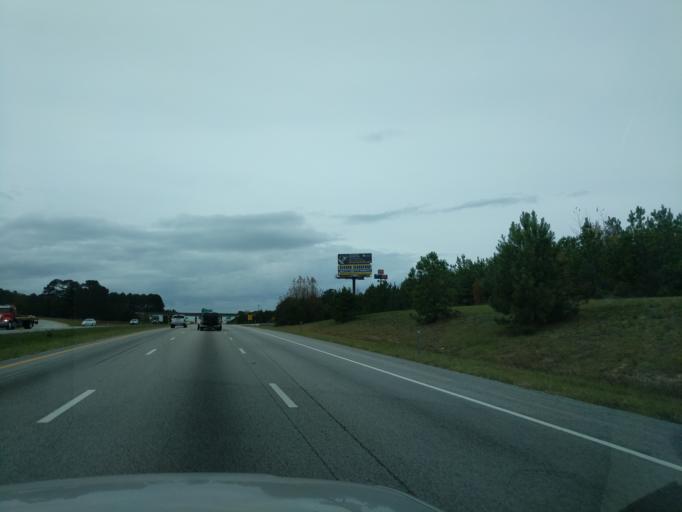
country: US
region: South Carolina
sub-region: Laurens County
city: Clinton
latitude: 34.5047
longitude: -81.8562
